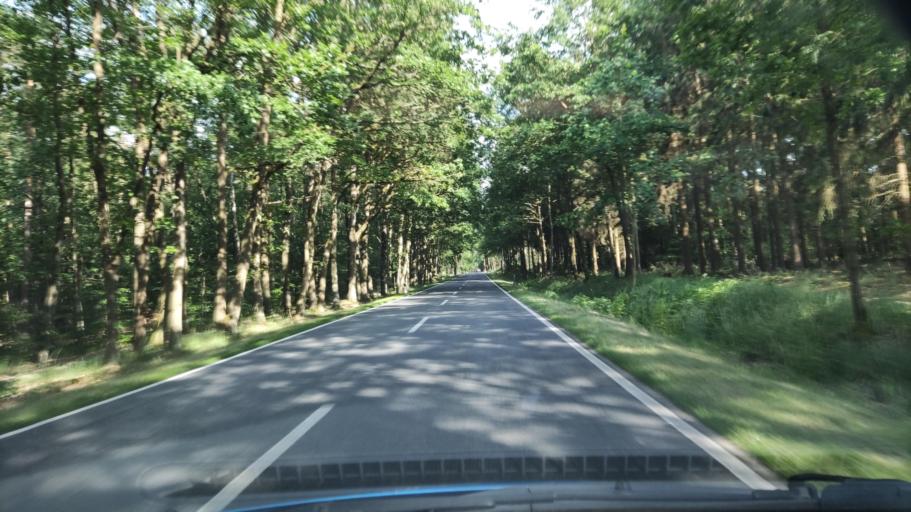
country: DE
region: Saxony-Anhalt
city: Klotze
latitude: 52.6135
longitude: 11.2019
